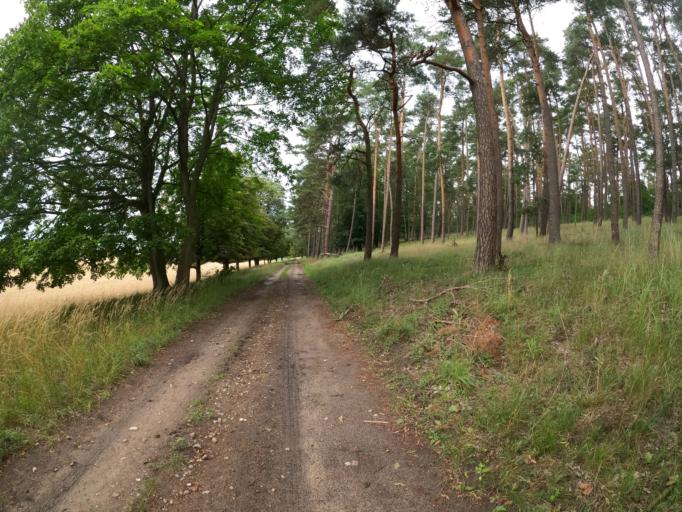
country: DE
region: Brandenburg
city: Althuttendorf
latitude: 53.0315
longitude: 13.8892
